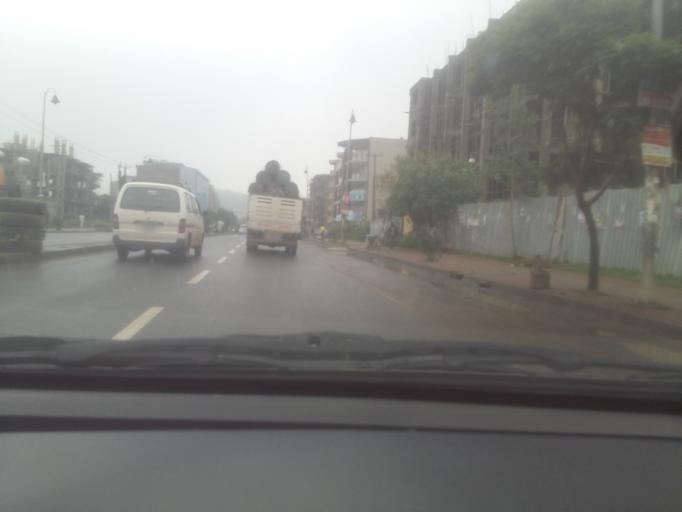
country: ET
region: Adis Abeba
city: Addis Ababa
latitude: 8.9514
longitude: 38.7176
